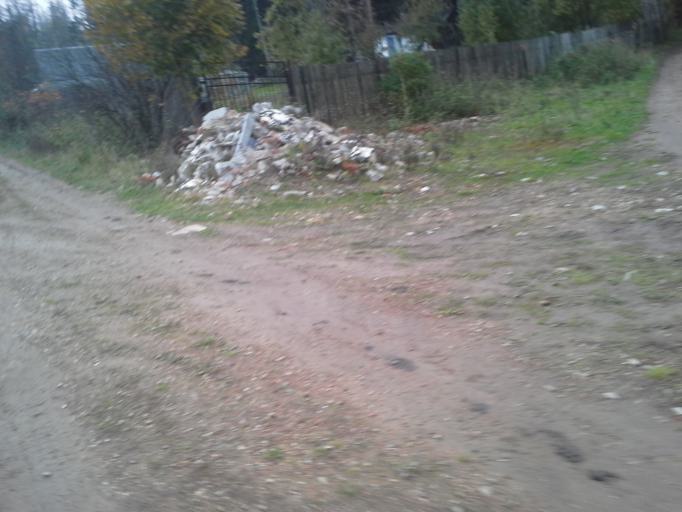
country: RU
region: Moskovskaya
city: Nazar'yevo
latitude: 55.6910
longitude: 37.0158
